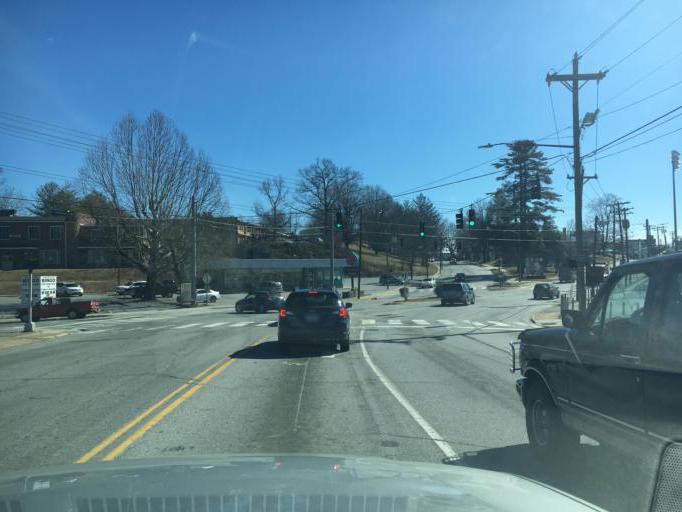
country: US
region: North Carolina
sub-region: Henderson County
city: Hendersonville
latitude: 35.3236
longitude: -82.4633
